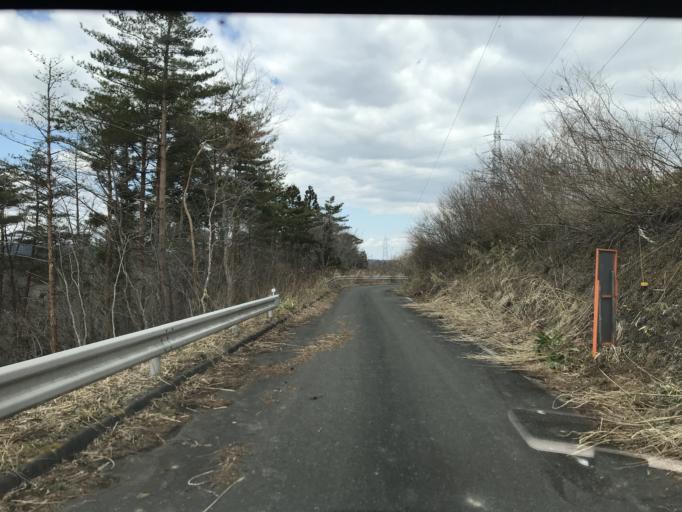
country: JP
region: Iwate
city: Ichinoseki
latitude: 38.9539
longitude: 141.0718
